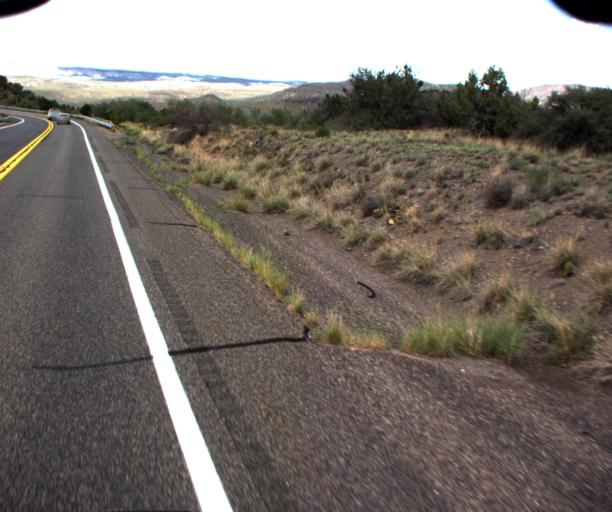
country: US
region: Arizona
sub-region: Yavapai County
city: Lake Montezuma
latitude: 34.5022
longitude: -111.7223
